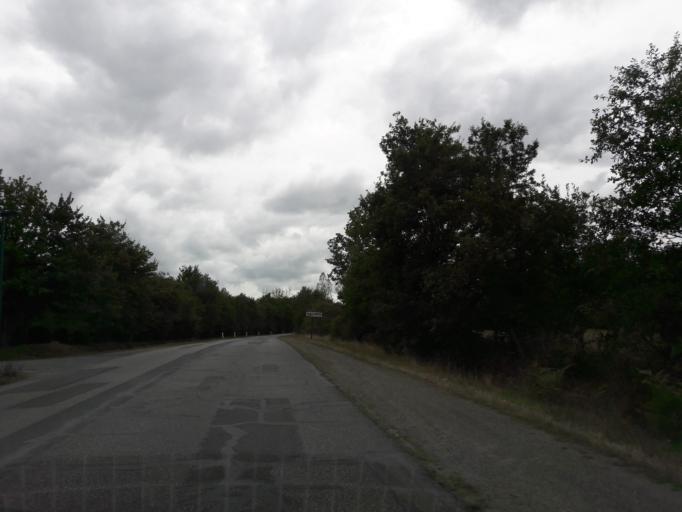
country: FR
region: Brittany
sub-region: Departement d'Ille-et-Vilaine
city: Orgeres
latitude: 48.0044
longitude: -1.6975
